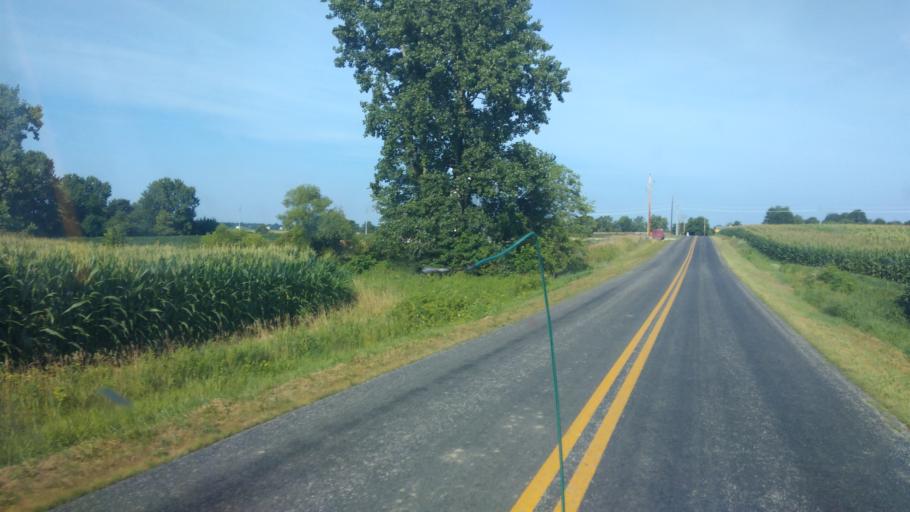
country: US
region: Ohio
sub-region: Delaware County
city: Delaware
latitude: 40.3397
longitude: -83.0171
